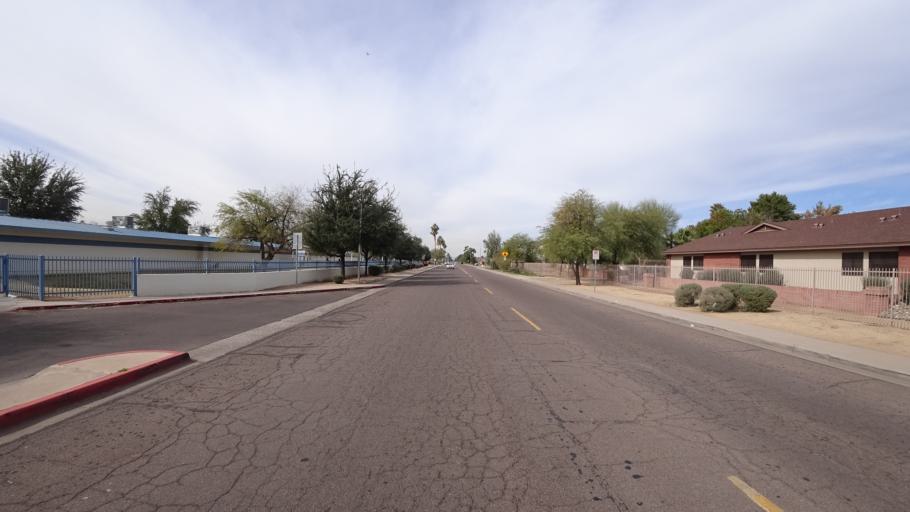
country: US
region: Arizona
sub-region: Maricopa County
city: Glendale
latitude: 33.5312
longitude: -112.1415
